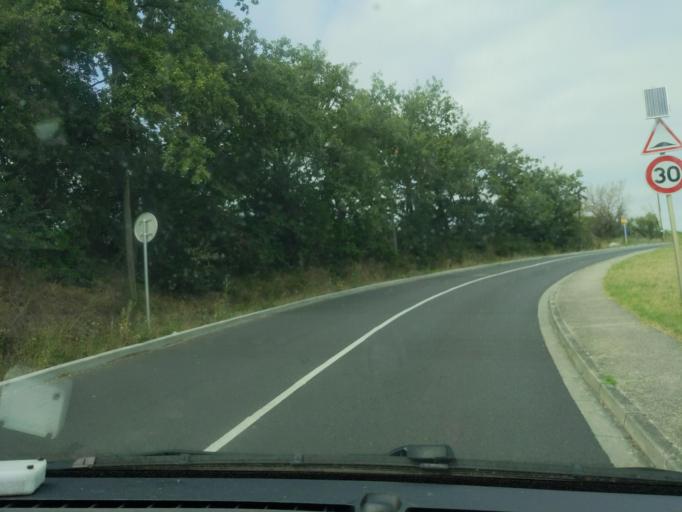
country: FR
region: Midi-Pyrenees
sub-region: Departement de la Haute-Garonne
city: Labege
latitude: 43.5407
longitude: 1.5314
